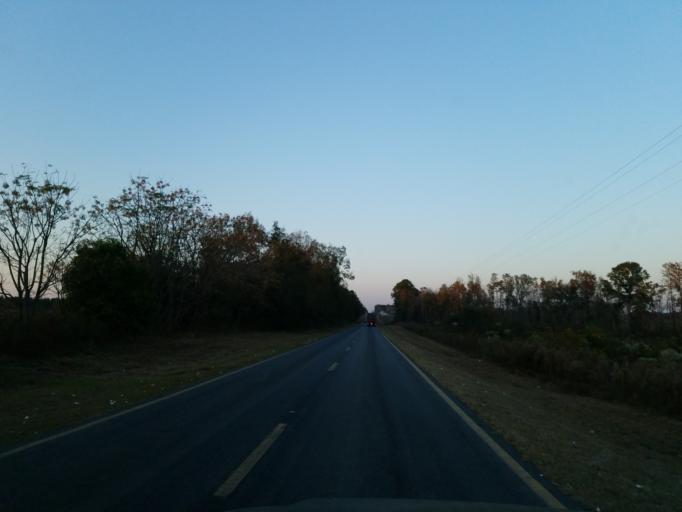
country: US
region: Georgia
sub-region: Ben Hill County
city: Fitzgerald
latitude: 31.7123
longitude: -83.3849
